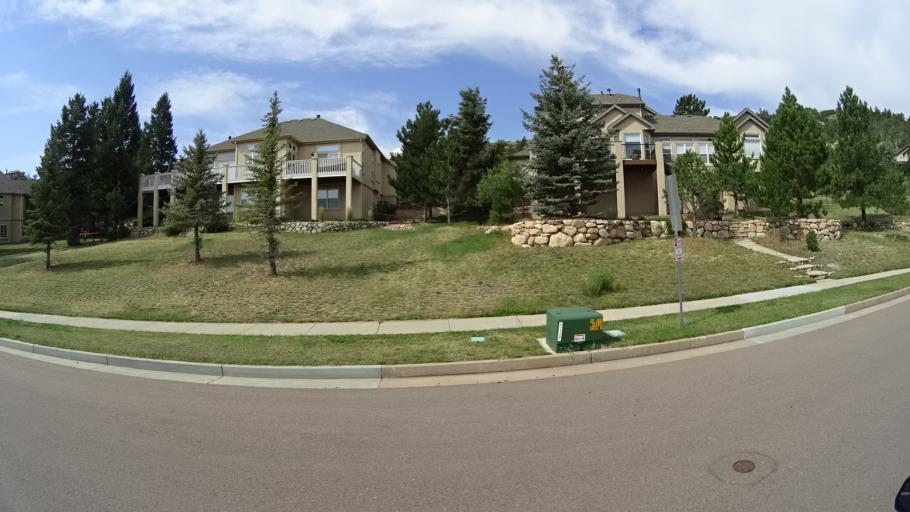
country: US
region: Colorado
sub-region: El Paso County
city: Air Force Academy
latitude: 38.9439
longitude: -104.8698
